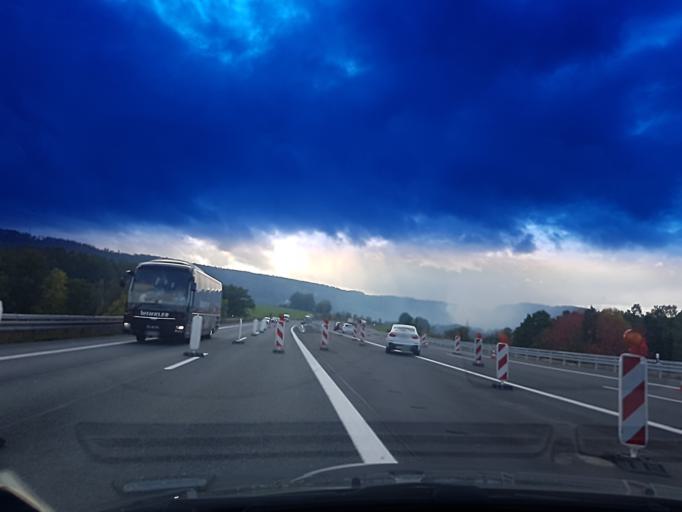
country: DE
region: Bavaria
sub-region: Upper Franconia
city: Thurnau
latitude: 50.0183
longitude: 11.4023
